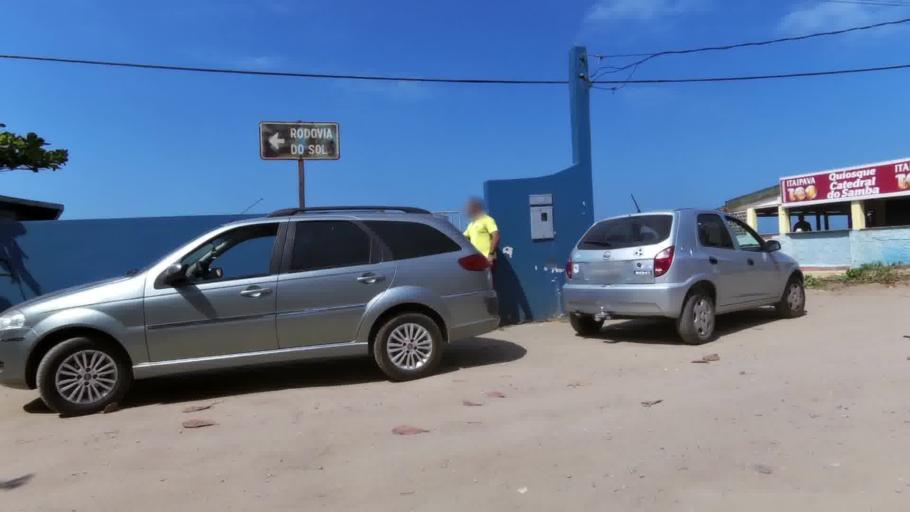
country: BR
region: Espirito Santo
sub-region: Marataizes
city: Marataizes
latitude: -21.0369
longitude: -40.8180
